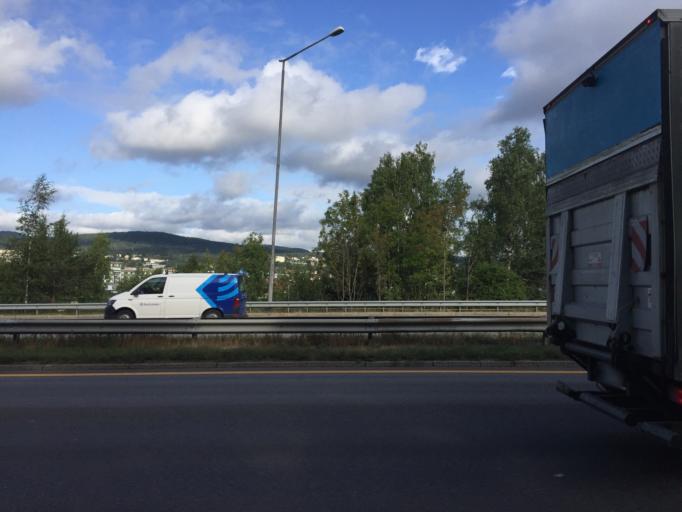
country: NO
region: Akershus
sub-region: Lorenskog
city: Kjenn
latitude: 59.9346
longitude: 10.8802
